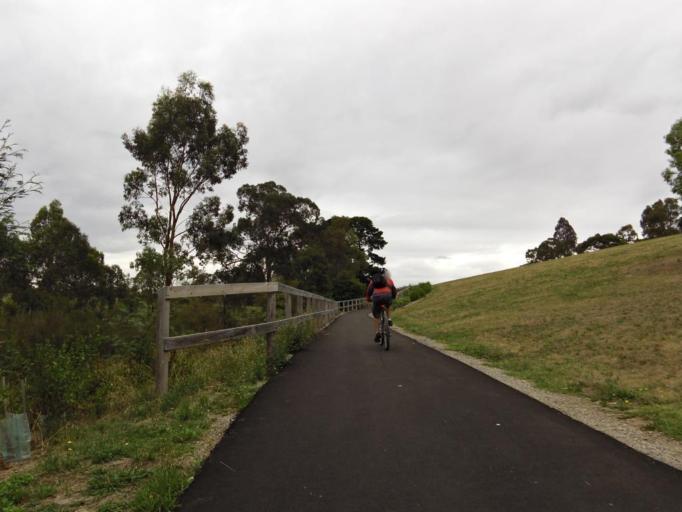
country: AU
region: Victoria
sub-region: Manningham
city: Templestowe Lower
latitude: -37.7719
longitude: 145.1351
